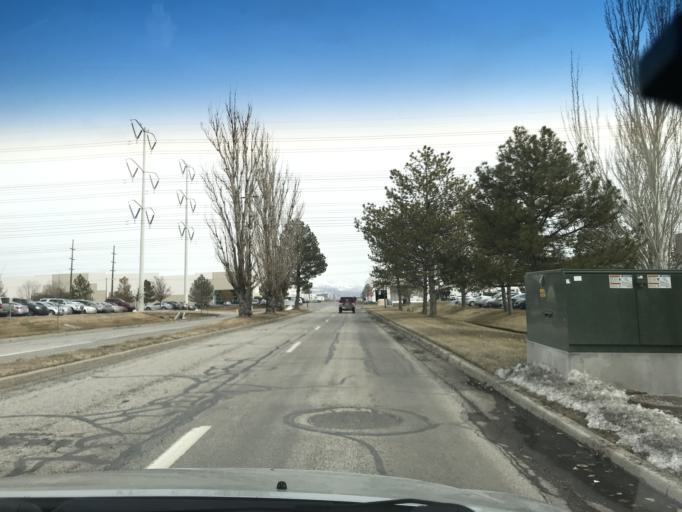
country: US
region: Utah
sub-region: Salt Lake County
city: West Valley City
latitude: 40.7813
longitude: -112.0076
